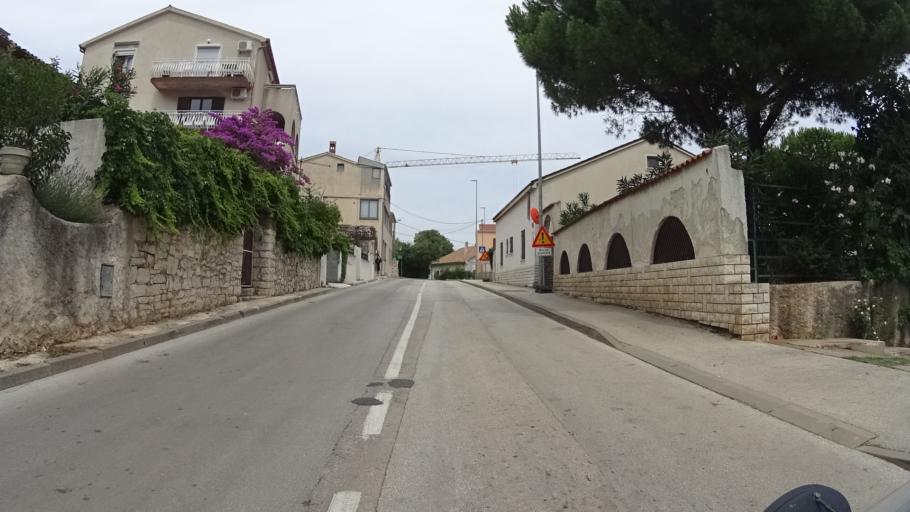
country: HR
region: Istarska
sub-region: Grad Pula
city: Pula
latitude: 44.8615
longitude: 13.8177
